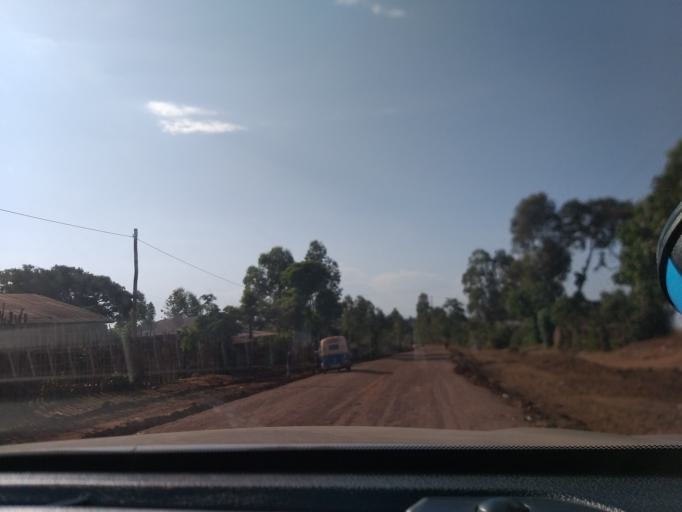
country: ET
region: Oromiya
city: Shashemene
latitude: 7.4271
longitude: 38.8111
